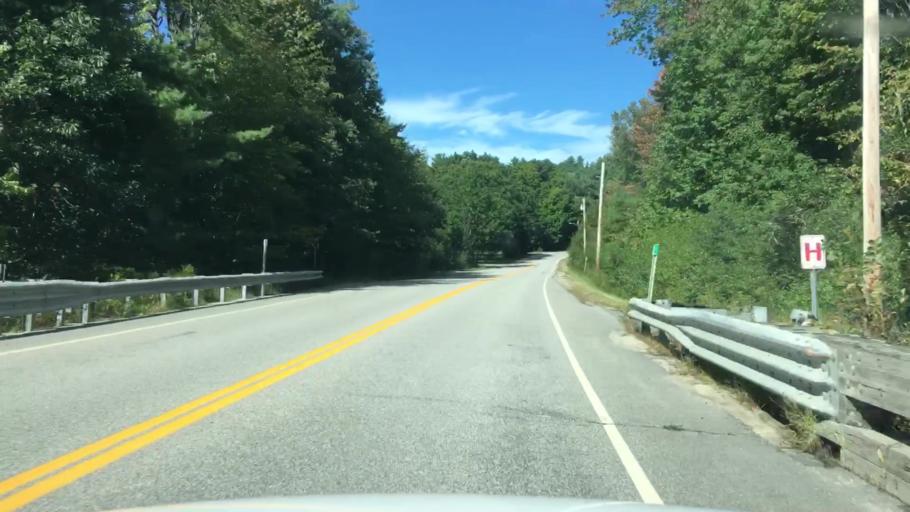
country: US
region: Maine
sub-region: Cumberland County
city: West Scarborough
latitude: 43.6277
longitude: -70.4088
